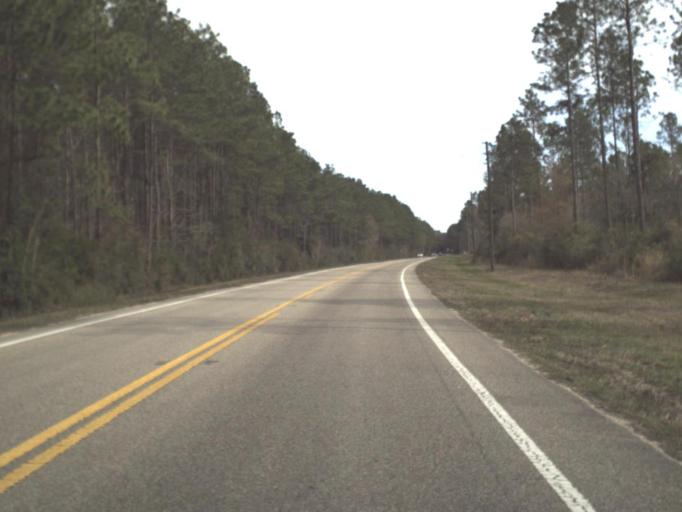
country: US
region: Florida
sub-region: Leon County
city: Woodville
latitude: 30.2077
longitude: -84.1903
